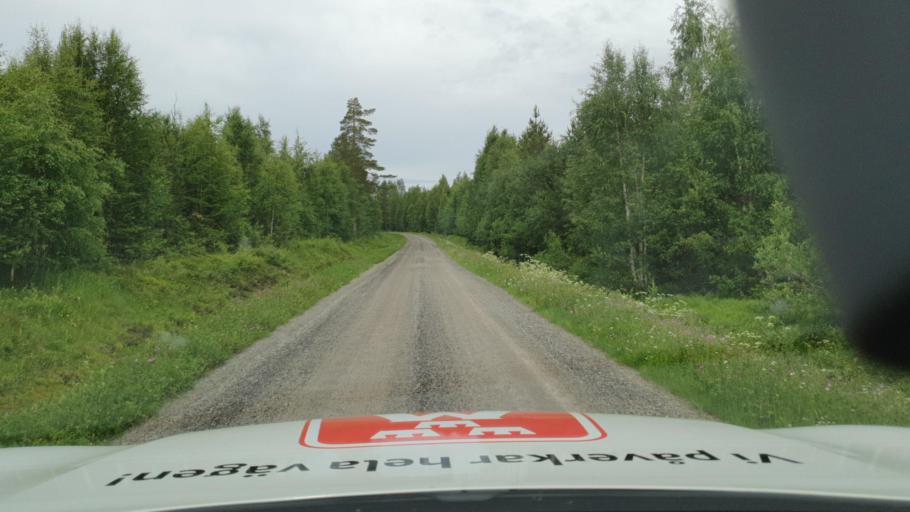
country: SE
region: Vaesterbotten
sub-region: Robertsfors Kommun
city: Robertsfors
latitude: 64.1976
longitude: 20.7086
